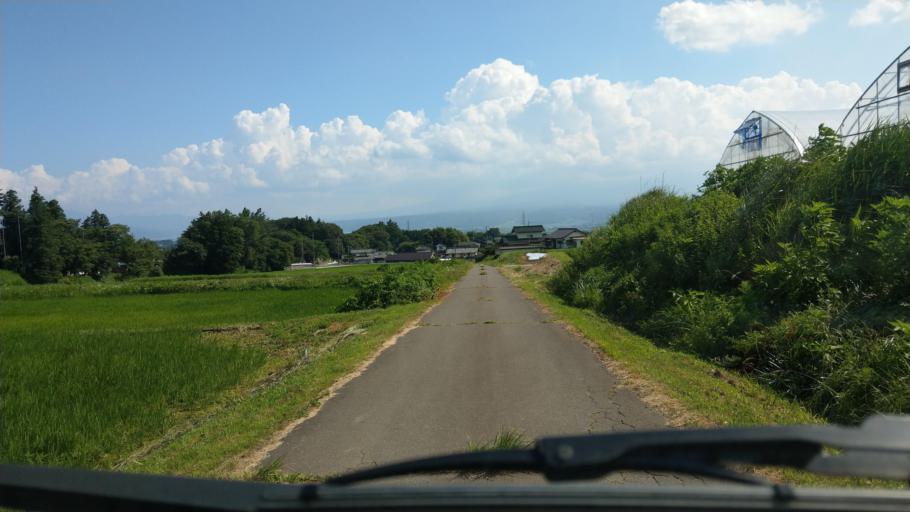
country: JP
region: Nagano
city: Komoro
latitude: 36.3252
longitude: 138.4500
